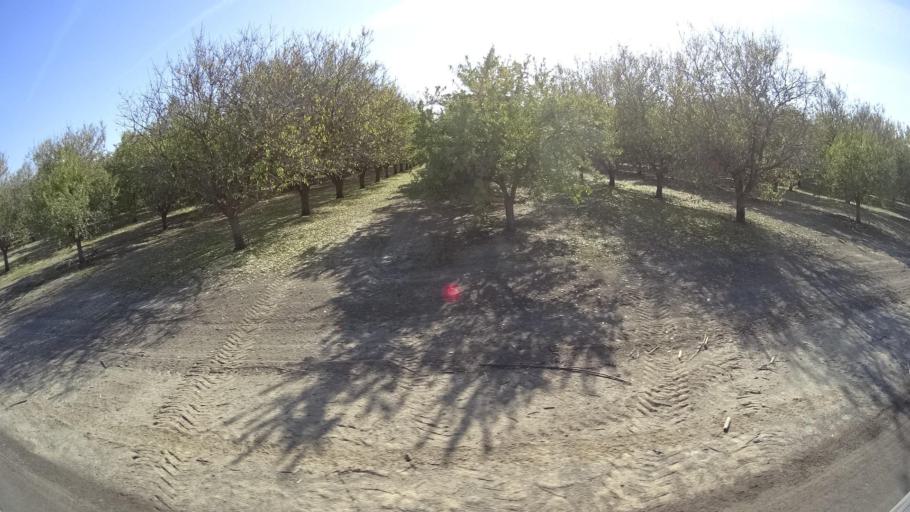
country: US
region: California
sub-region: Kern County
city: Wasco
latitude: 35.6597
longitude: -119.3965
